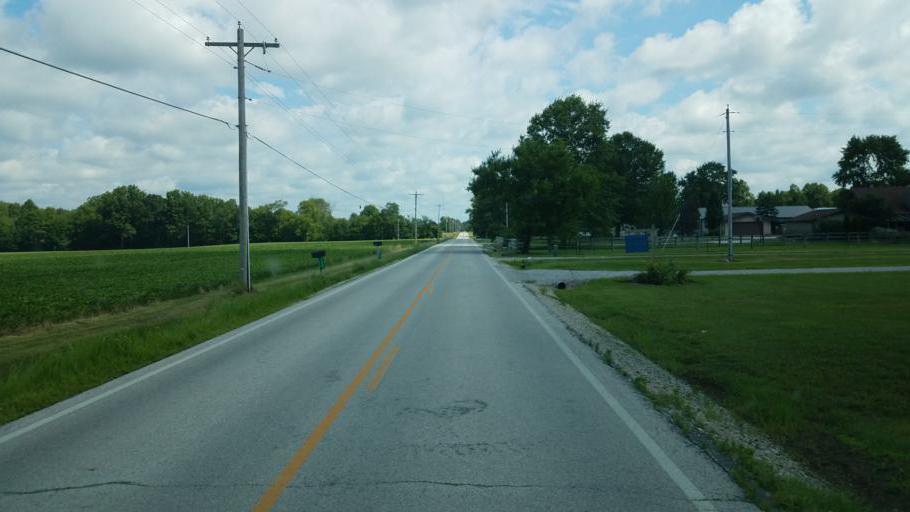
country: US
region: Ohio
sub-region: Delaware County
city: Ashley
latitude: 40.3187
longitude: -82.9327
